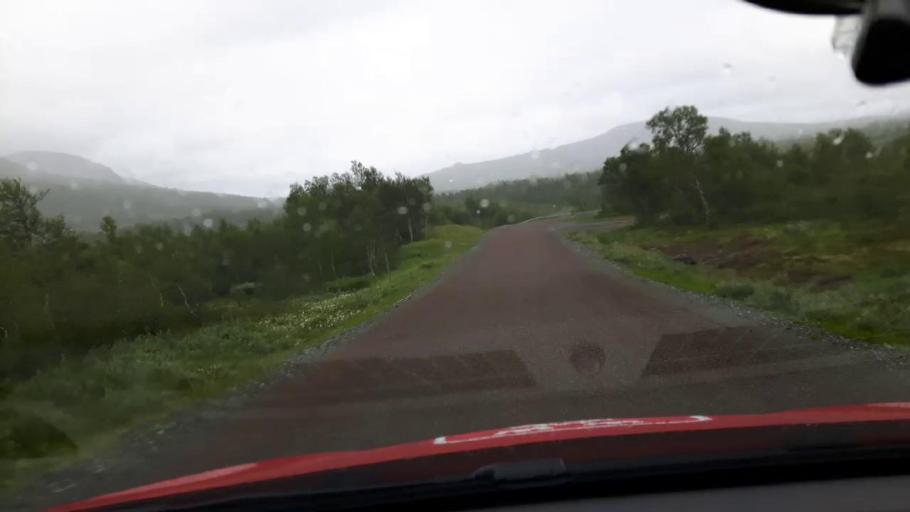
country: NO
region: Nord-Trondelag
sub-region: Meraker
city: Meraker
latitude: 63.1786
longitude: 12.3755
